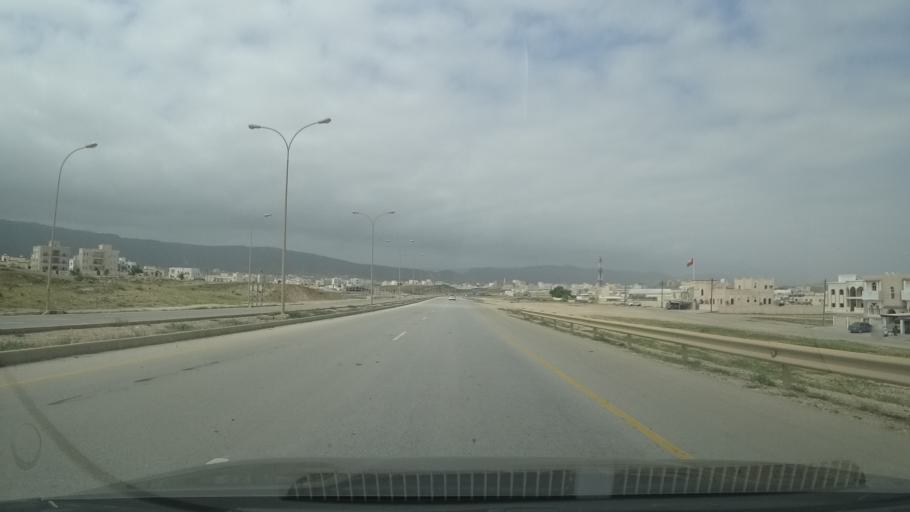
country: OM
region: Zufar
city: Salalah
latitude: 17.0480
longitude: 54.3839
